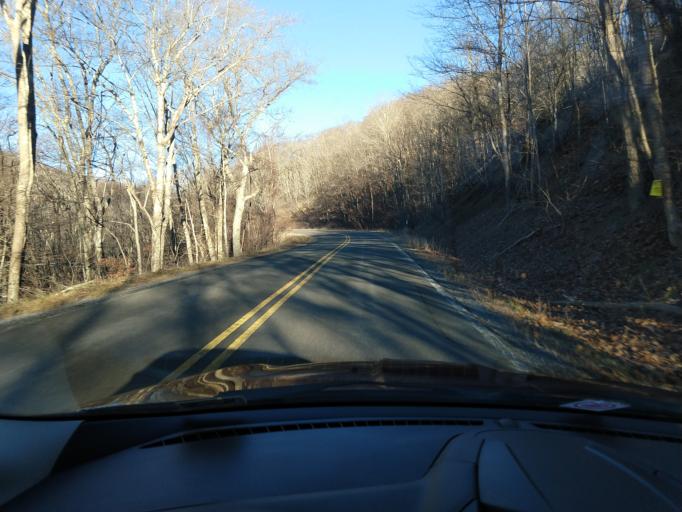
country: US
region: Virginia
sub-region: Highland County
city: Monterey
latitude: 38.4548
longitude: -79.6620
